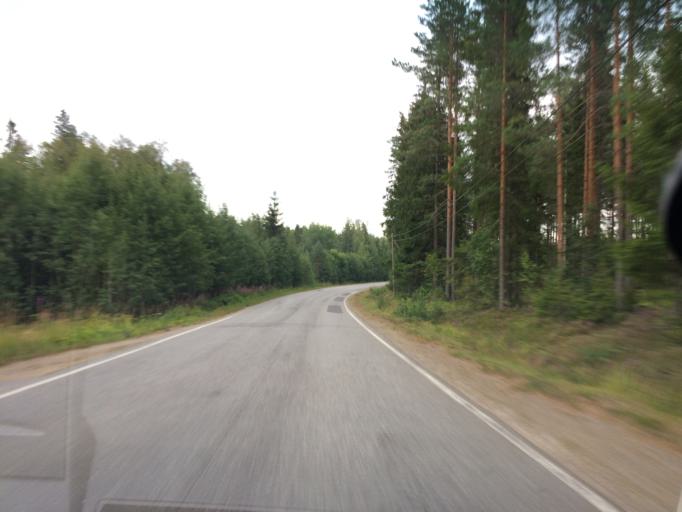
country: FI
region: Haeme
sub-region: Haemeenlinna
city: Tuulos
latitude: 61.2229
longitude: 24.7197
